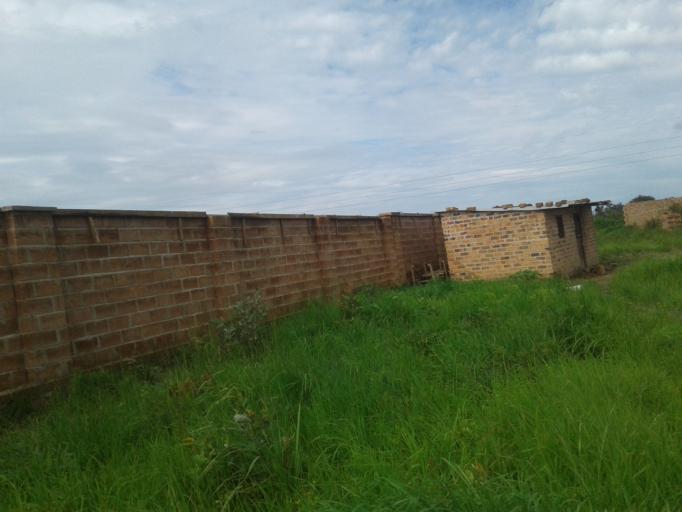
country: CD
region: Katanga
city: Lubumbashi
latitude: -11.4673
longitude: 27.5465
